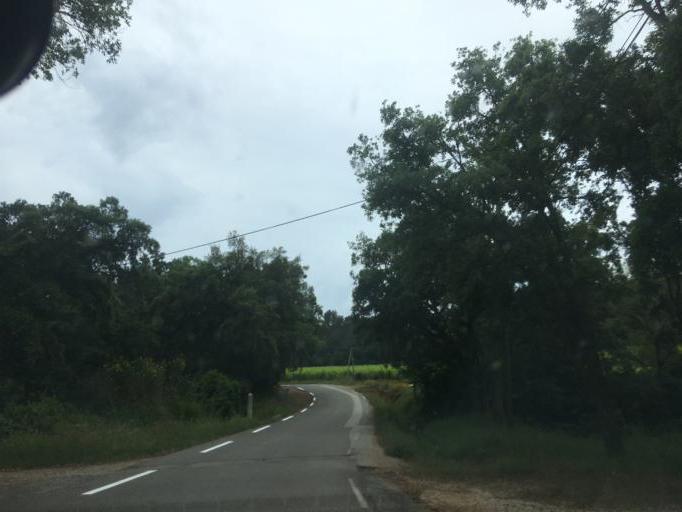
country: FR
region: Provence-Alpes-Cote d'Azur
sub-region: Departement du Var
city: La Londe-les-Maures
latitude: 43.1728
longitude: 6.2158
